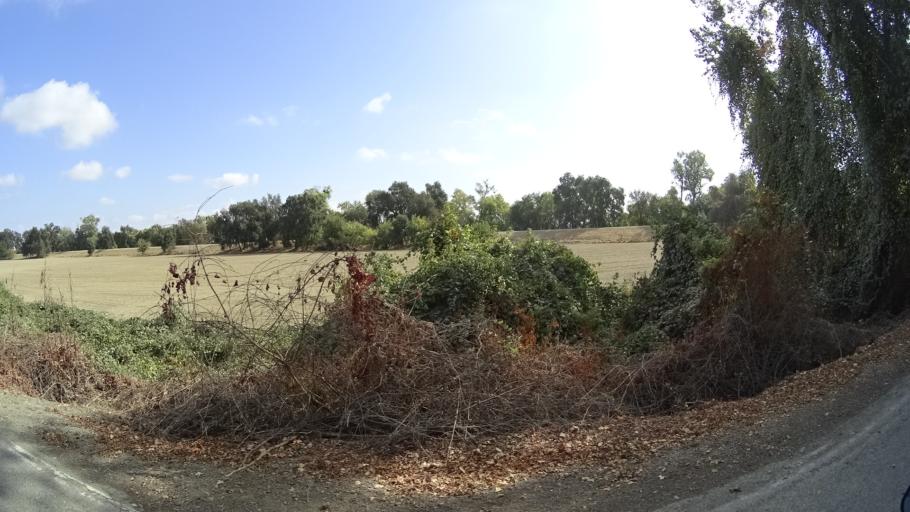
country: US
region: California
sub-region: Yolo County
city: Woodland
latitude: 38.7732
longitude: -121.6904
